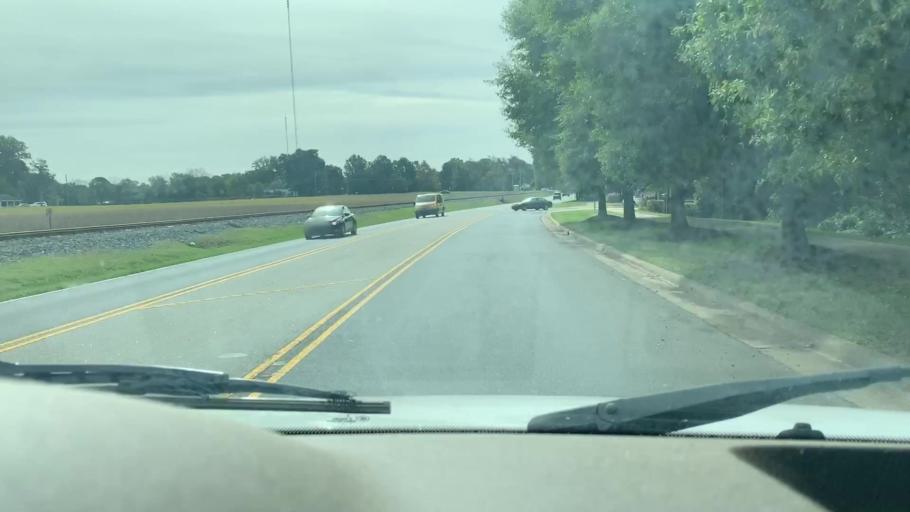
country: US
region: North Carolina
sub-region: Mecklenburg County
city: Cornelius
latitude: 35.4563
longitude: -80.8426
